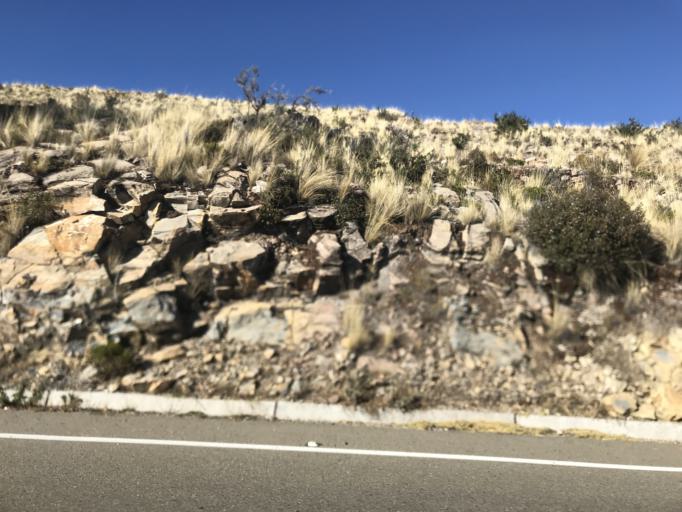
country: BO
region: La Paz
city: San Pedro
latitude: -16.1893
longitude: -68.9343
